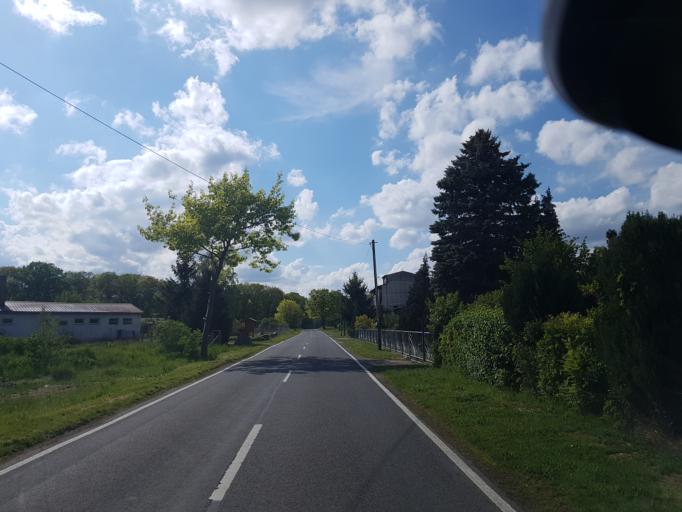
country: DE
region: Brandenburg
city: Spremberg
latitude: 51.6538
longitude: 14.3240
